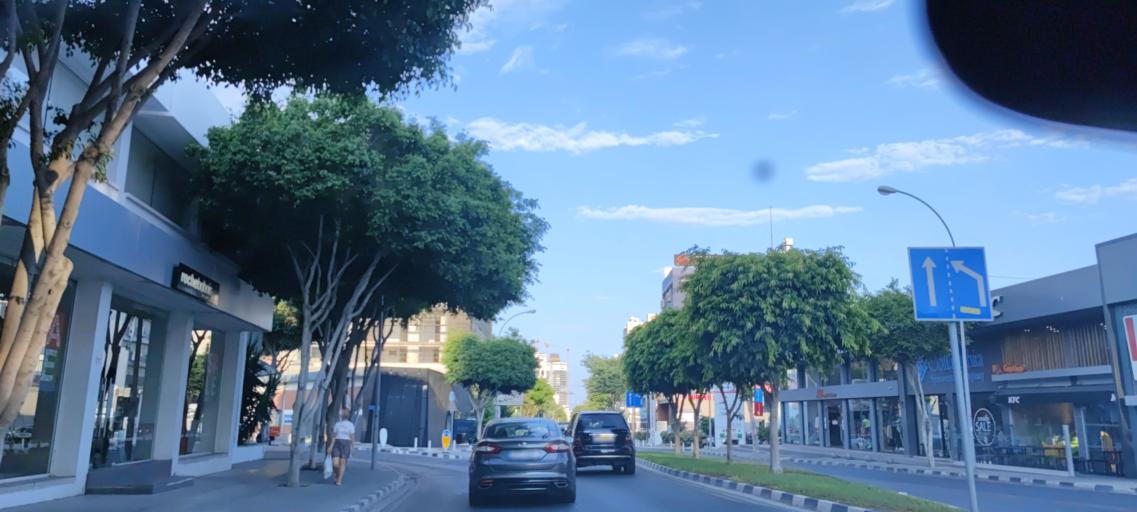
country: CY
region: Limassol
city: Limassol
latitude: 34.6878
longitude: 33.0452
